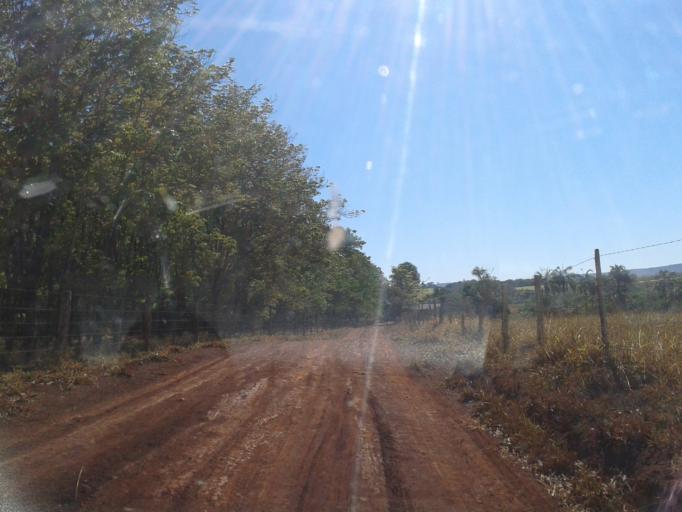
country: BR
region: Minas Gerais
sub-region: Centralina
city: Centralina
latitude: -18.5691
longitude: -49.1339
